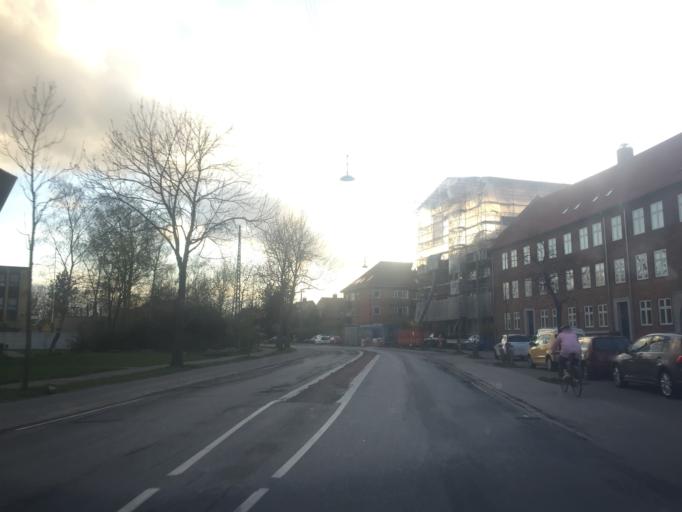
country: DK
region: Capital Region
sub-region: Hvidovre Kommune
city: Hvidovre
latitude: 55.6597
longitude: 12.4929
